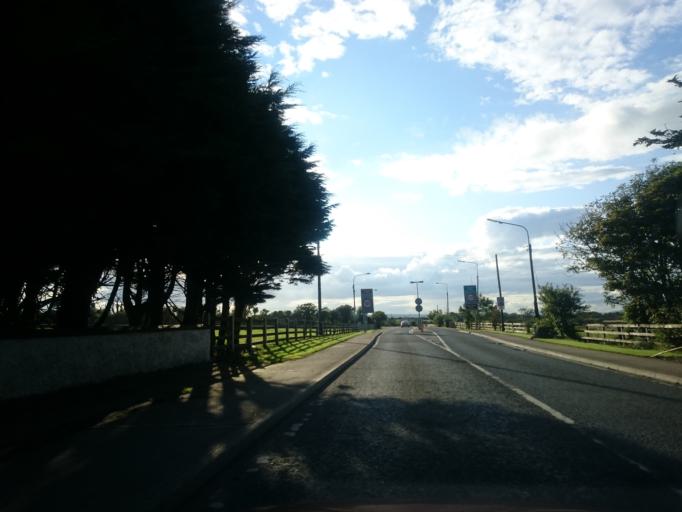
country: IE
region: Leinster
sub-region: Loch Garman
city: Ballygerry
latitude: 52.2425
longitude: -6.3576
